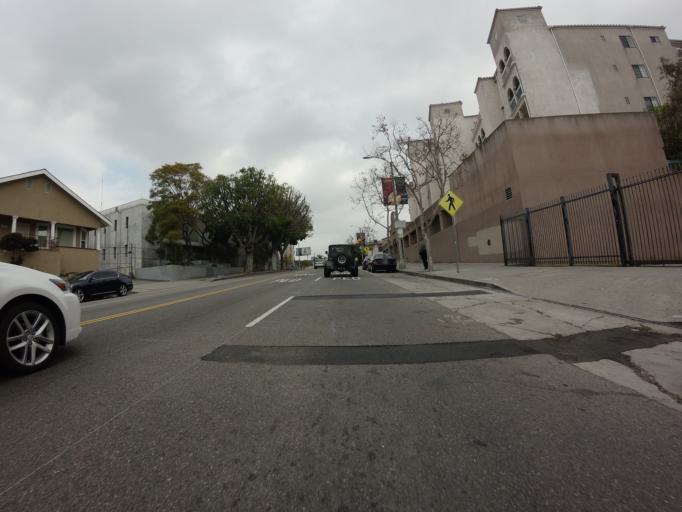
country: US
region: California
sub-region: Los Angeles County
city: Echo Park
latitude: 34.0677
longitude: -118.2587
